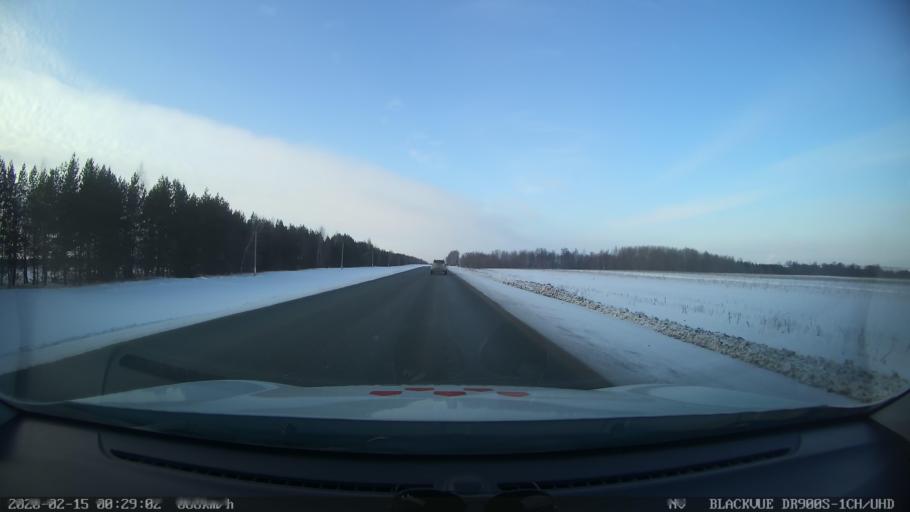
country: RU
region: Tatarstan
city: Verkhniy Uslon
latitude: 55.6472
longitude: 48.8729
